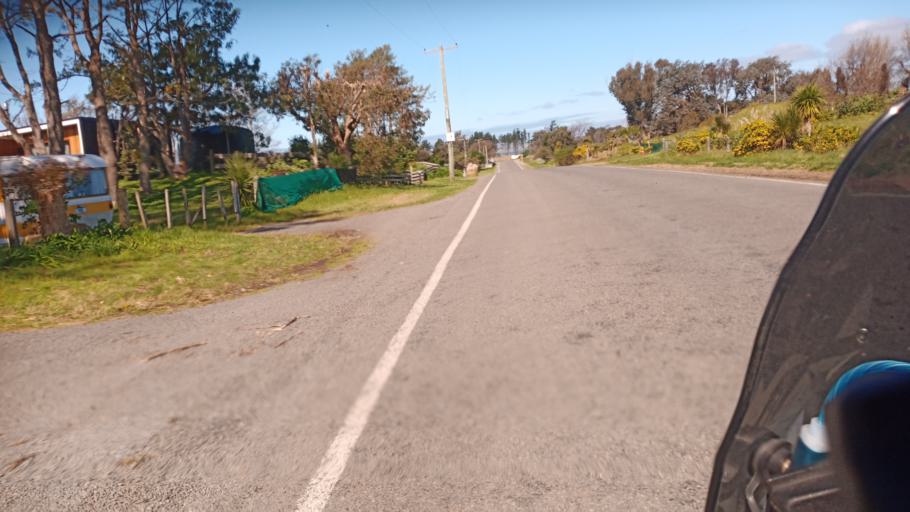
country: NZ
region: Gisborne
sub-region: Gisborne District
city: Gisborne
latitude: -39.0157
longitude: 177.8800
